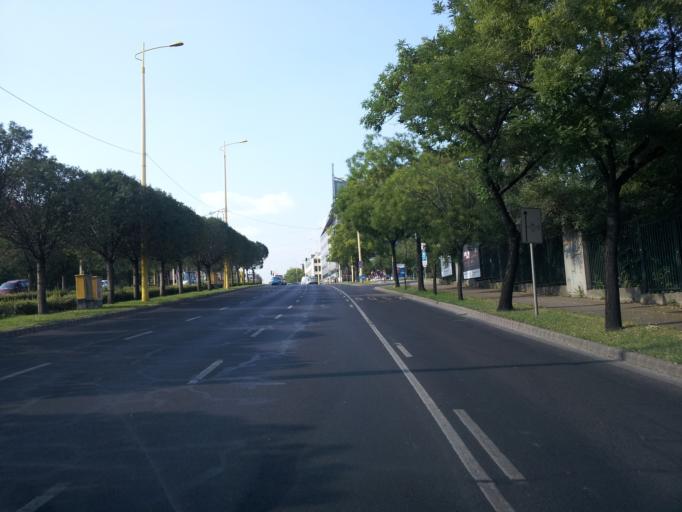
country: HU
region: Budapest
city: Budapest XII. keruelet
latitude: 47.4887
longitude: 19.0248
